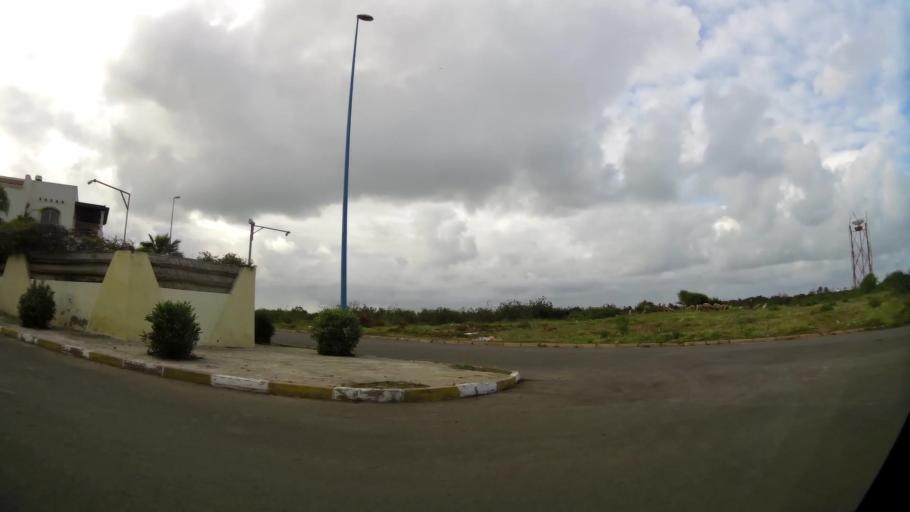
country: MA
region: Grand Casablanca
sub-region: Casablanca
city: Casablanca
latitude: 33.5790
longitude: -7.6929
